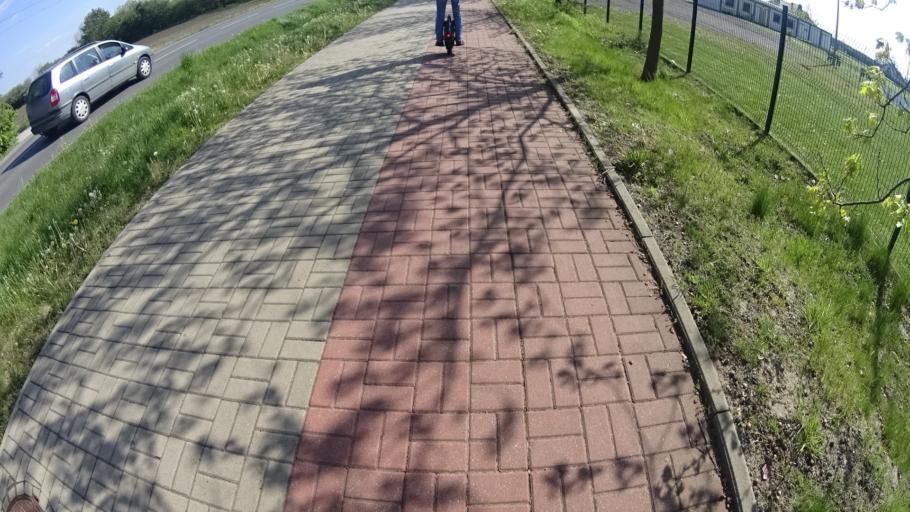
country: PL
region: Masovian Voivodeship
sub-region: Powiat warszawski zachodni
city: Stare Babice
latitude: 52.2442
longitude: 20.8188
